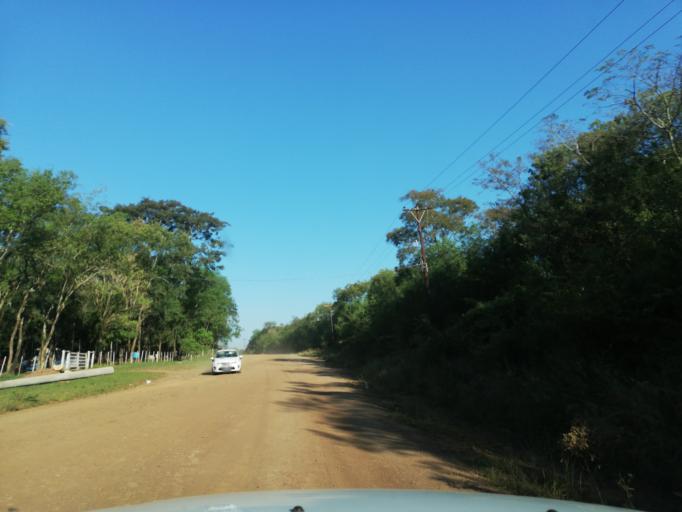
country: AR
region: Misiones
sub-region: Departamento de Candelaria
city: Candelaria
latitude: -27.5500
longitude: -55.7108
